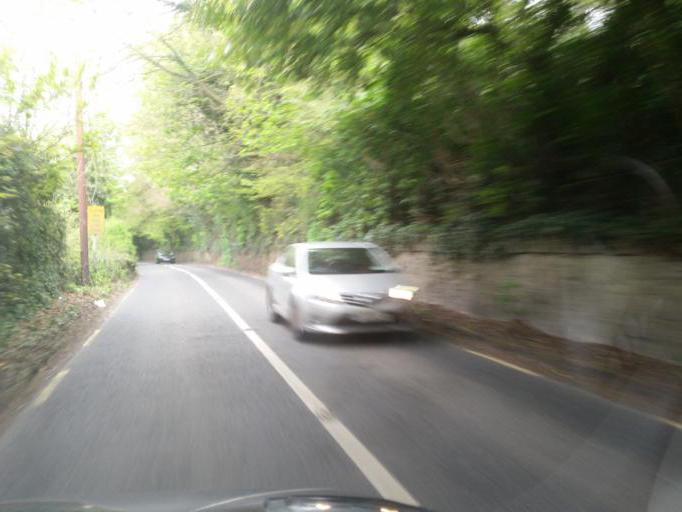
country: IE
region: Leinster
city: Castleknock
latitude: 53.3777
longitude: -6.3366
